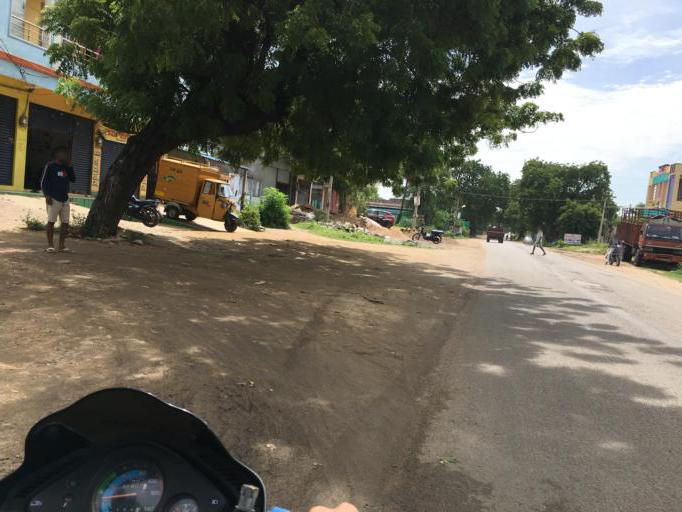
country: IN
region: Telangana
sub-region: Nalgonda
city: Nalgonda
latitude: 17.1670
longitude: 79.4165
